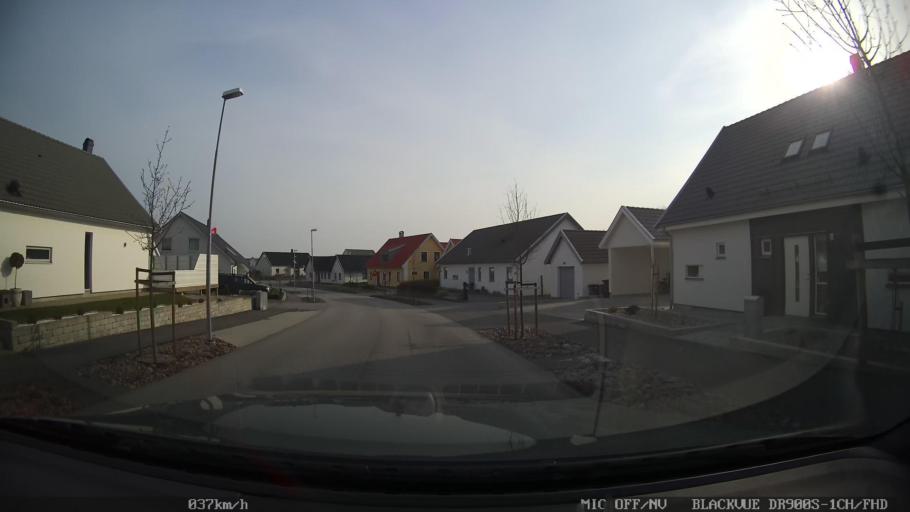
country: SE
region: Skane
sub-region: Ystads Kommun
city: Ystad
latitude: 55.4455
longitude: 13.7947
